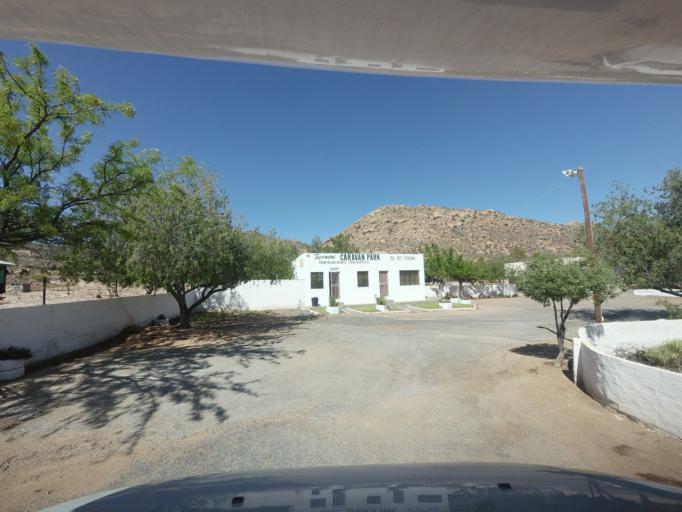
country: ZA
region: Northern Cape
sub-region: Namakwa District Municipality
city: Springbok
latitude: -29.6734
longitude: 17.8988
